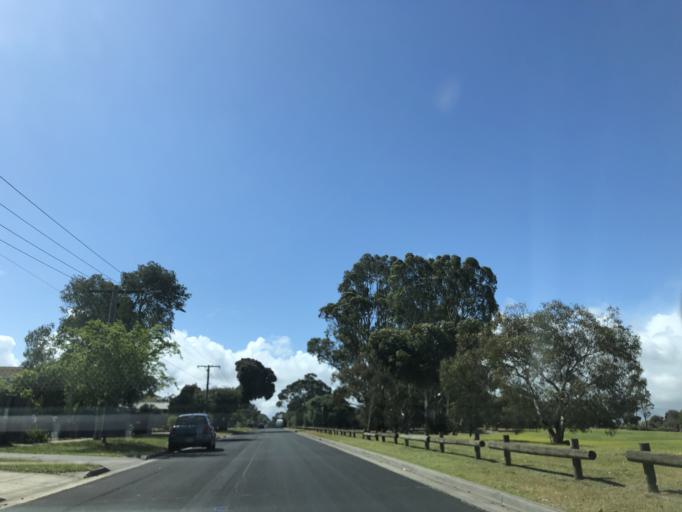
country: AU
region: Victoria
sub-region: Monash
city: Oakleigh South
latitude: -37.9327
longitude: 145.1020
